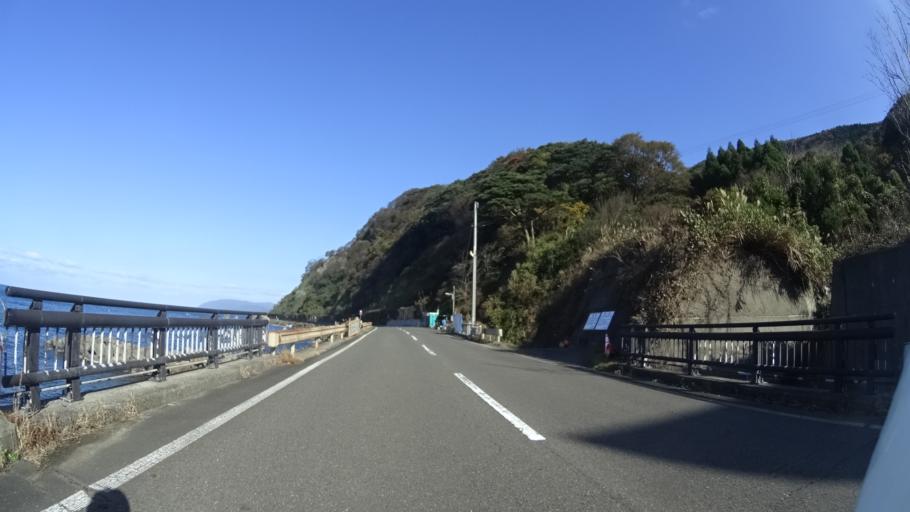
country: JP
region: Fukui
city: Tsuruga
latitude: 35.7570
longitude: 136.1017
